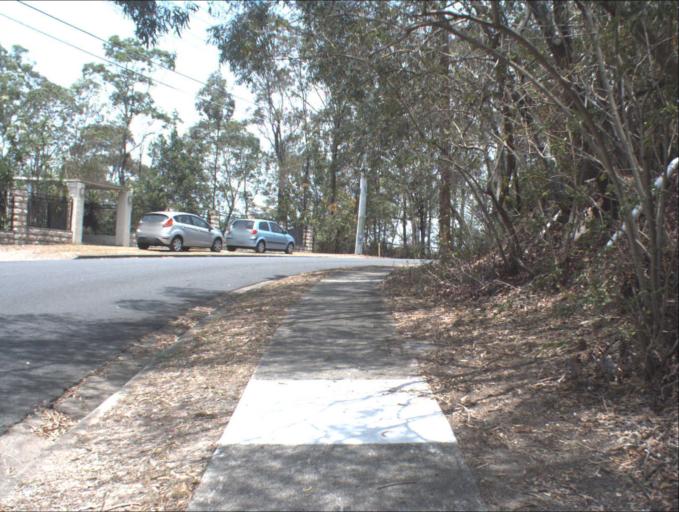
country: AU
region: Queensland
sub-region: Logan
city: Beenleigh
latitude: -27.6641
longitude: 153.1996
